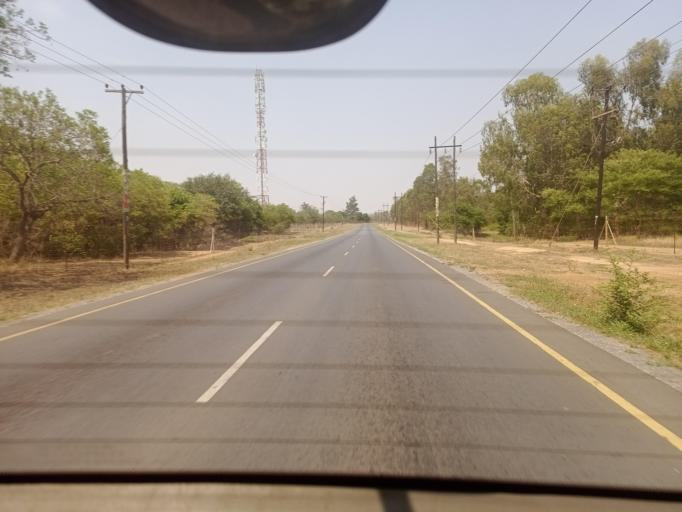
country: ZM
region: Lusaka
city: Lusaka
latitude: -15.2857
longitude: 28.3823
